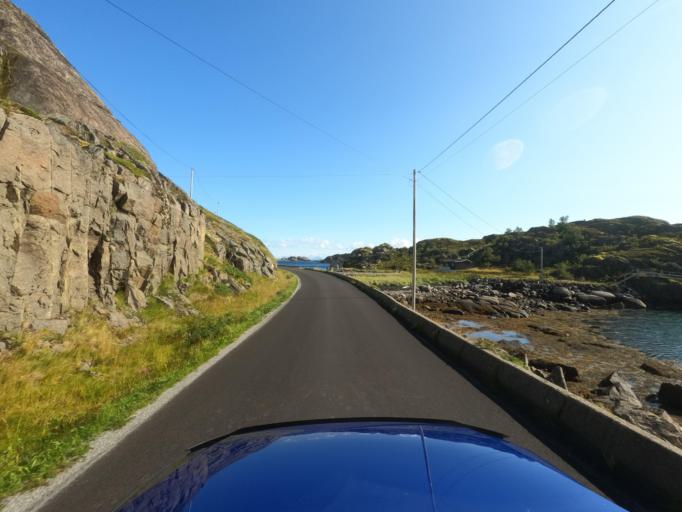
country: NO
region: Nordland
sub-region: Vestvagoy
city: Evjen
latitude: 68.1165
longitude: 13.8012
